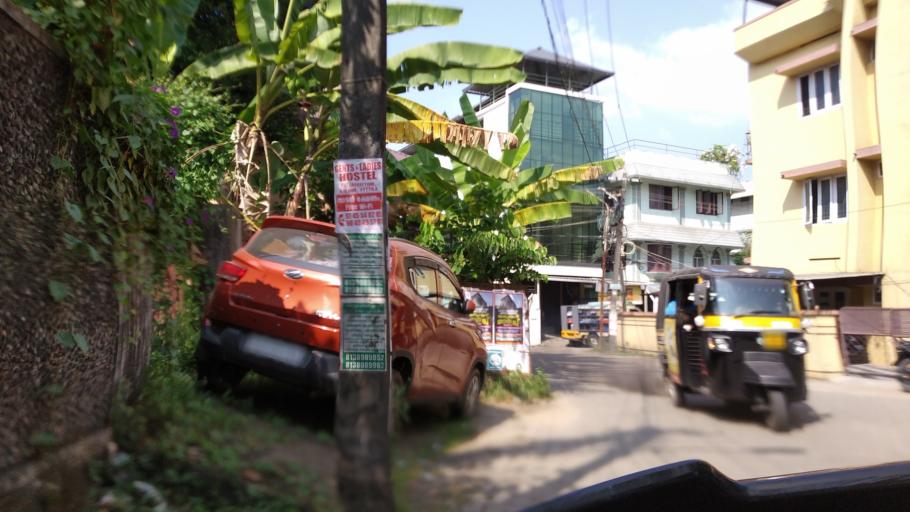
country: IN
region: Kerala
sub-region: Ernakulam
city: Cochin
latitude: 9.9738
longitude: 76.2893
